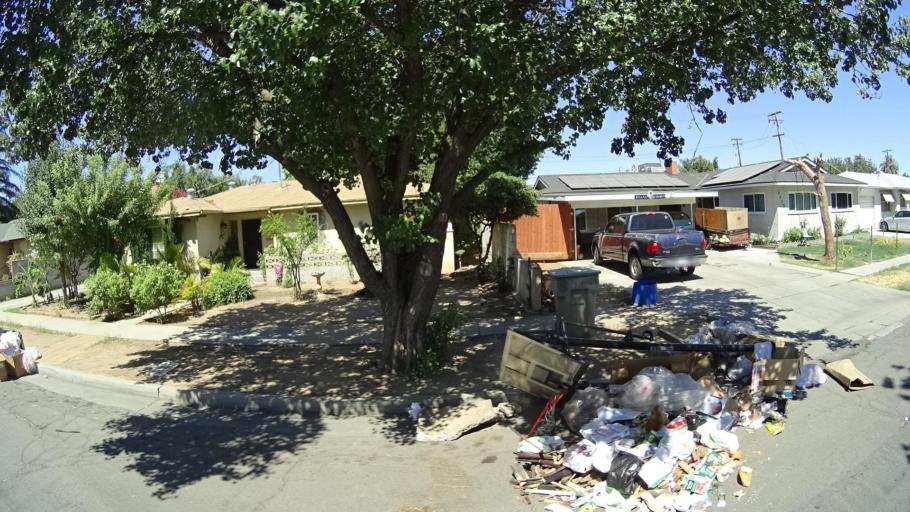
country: US
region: California
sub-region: Fresno County
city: Fresno
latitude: 36.7830
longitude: -119.7869
